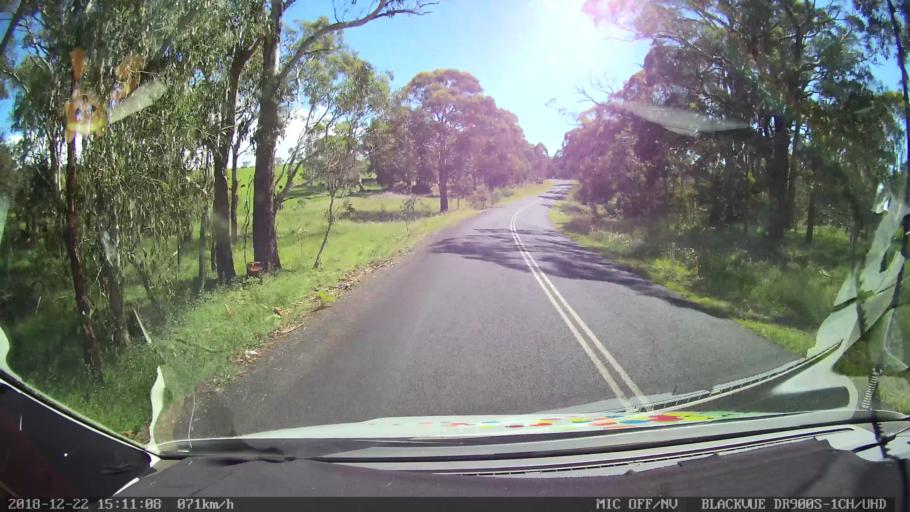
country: AU
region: New South Wales
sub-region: Bellingen
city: Dorrigo
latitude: -30.3414
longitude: 152.4049
